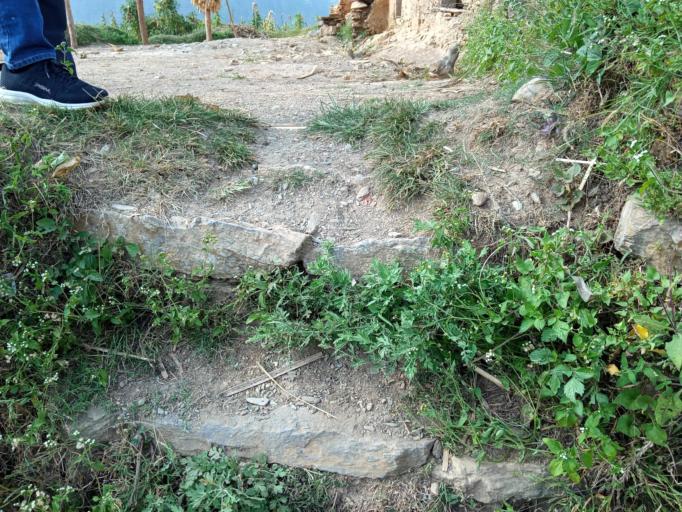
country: NP
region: Far Western
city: Dipayal
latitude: 29.5579
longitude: 80.8686
